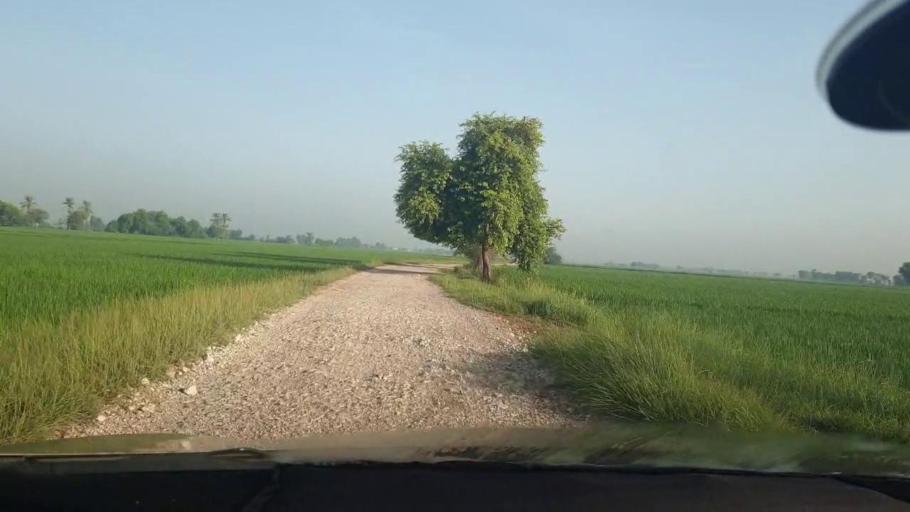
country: PK
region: Sindh
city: Kambar
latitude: 27.6188
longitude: 68.0190
